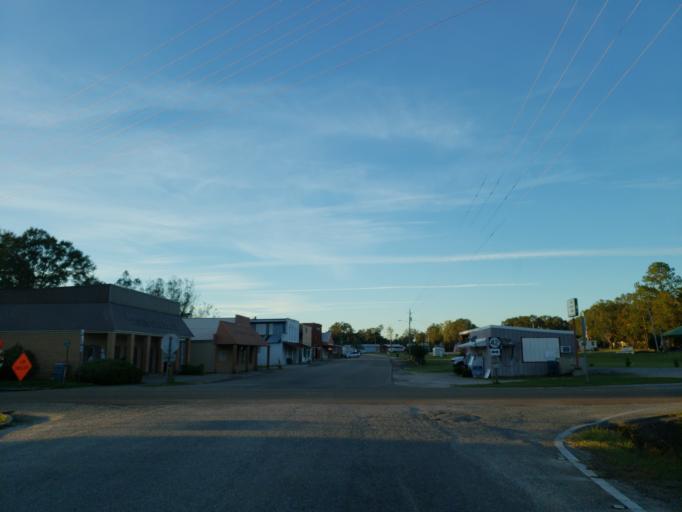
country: US
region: Mississippi
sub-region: Wayne County
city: Belmont
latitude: 31.4346
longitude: -88.4733
